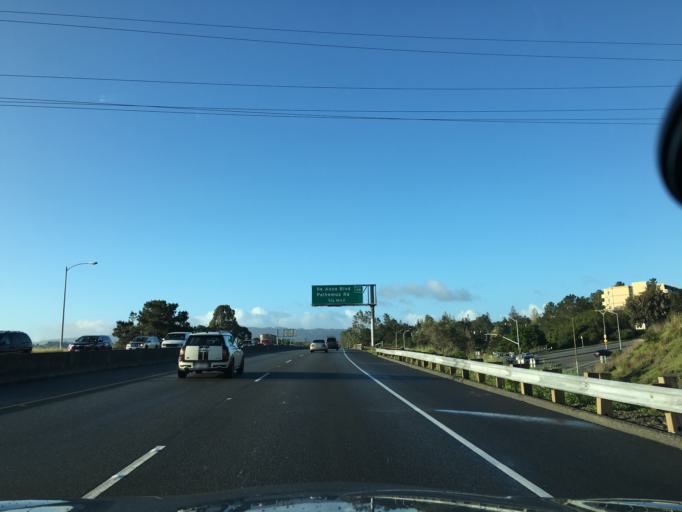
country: US
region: California
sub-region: San Mateo County
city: Highlands-Baywood Park
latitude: 37.5335
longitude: -122.3295
